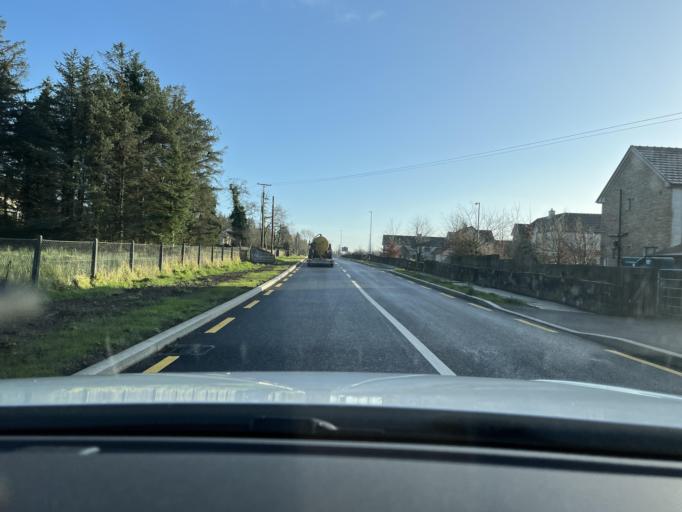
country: IE
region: Connaught
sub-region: County Leitrim
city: Manorhamilton
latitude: 54.1738
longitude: -8.1509
